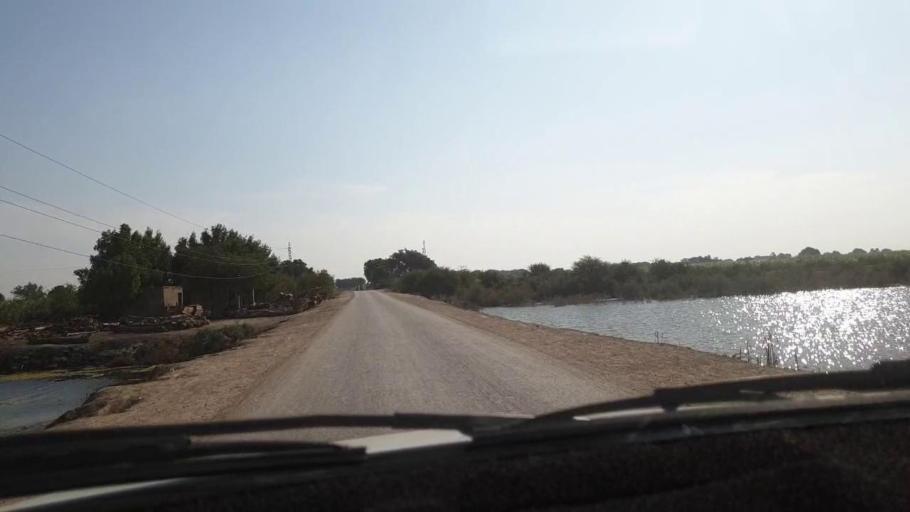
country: PK
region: Sindh
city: Bulri
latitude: 24.9660
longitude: 68.4204
